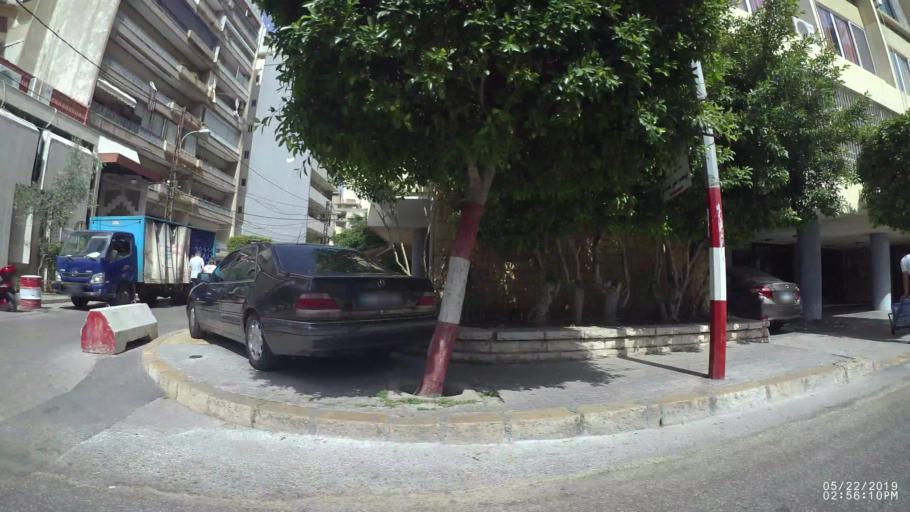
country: LB
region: Beyrouth
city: Ra's Bayrut
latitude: 33.8921
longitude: 35.4832
